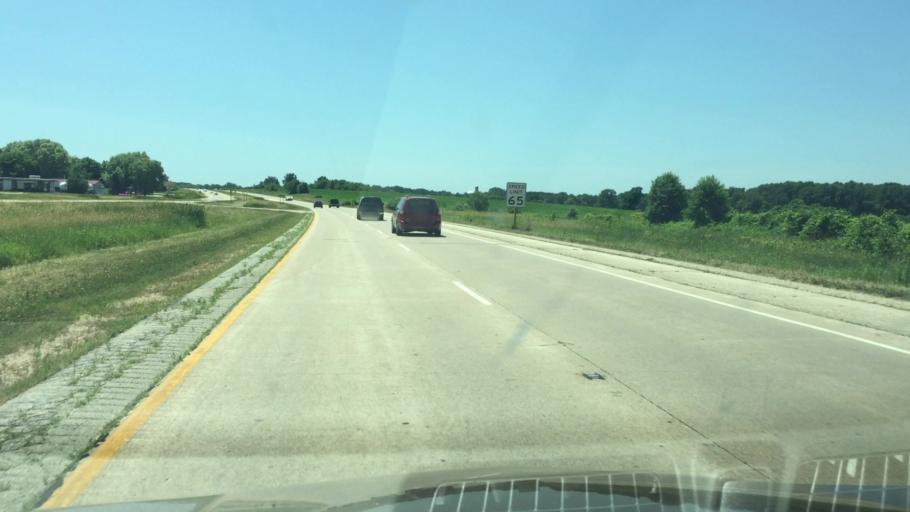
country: US
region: Wisconsin
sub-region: Dodge County
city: Beaver Dam
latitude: 43.4255
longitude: -88.8960
